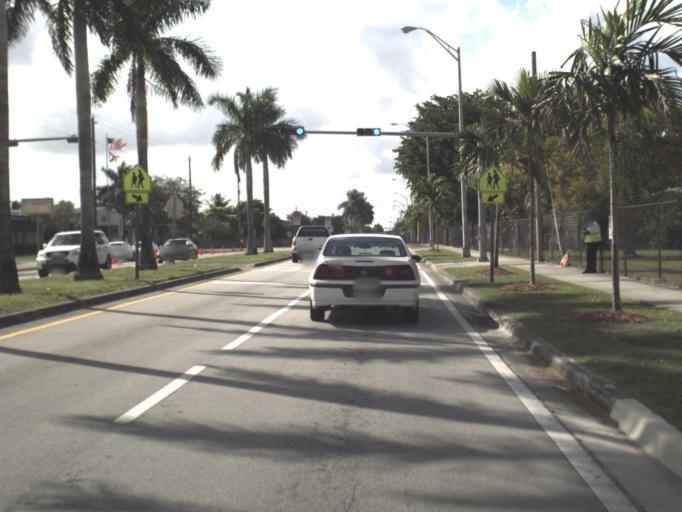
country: US
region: Florida
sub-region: Miami-Dade County
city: Leisure City
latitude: 25.4995
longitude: -80.4331
